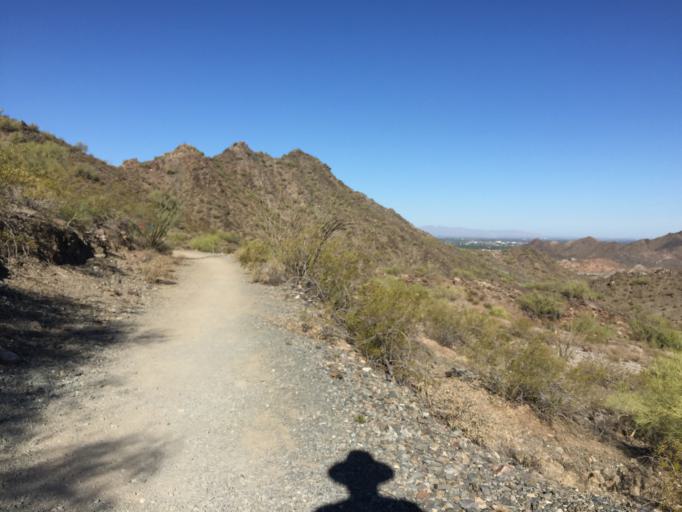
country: US
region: Arizona
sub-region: Maricopa County
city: Paradise Valley
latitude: 33.5574
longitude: -112.0194
